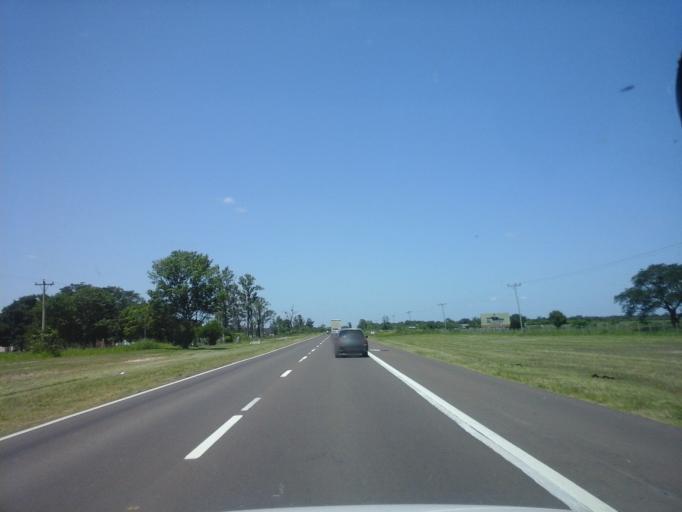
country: AR
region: Corrientes
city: Paso de la Patria
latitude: -27.4081
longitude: -58.6535
